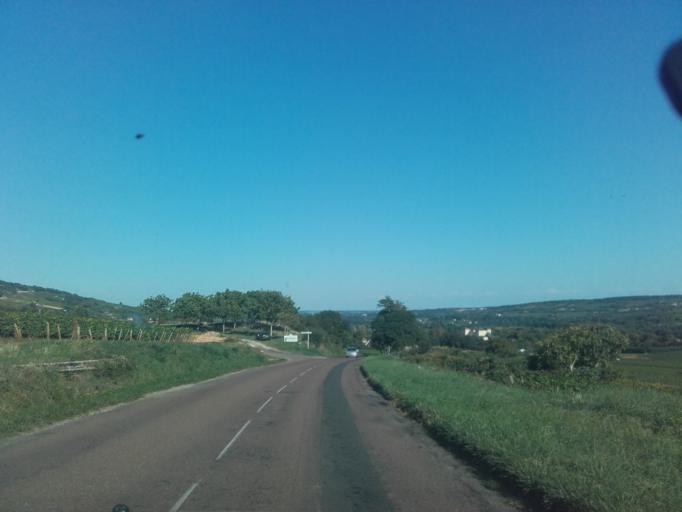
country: FR
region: Bourgogne
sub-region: Departement de la Cote-d'Or
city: Nolay
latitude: 46.9092
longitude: 4.6739
